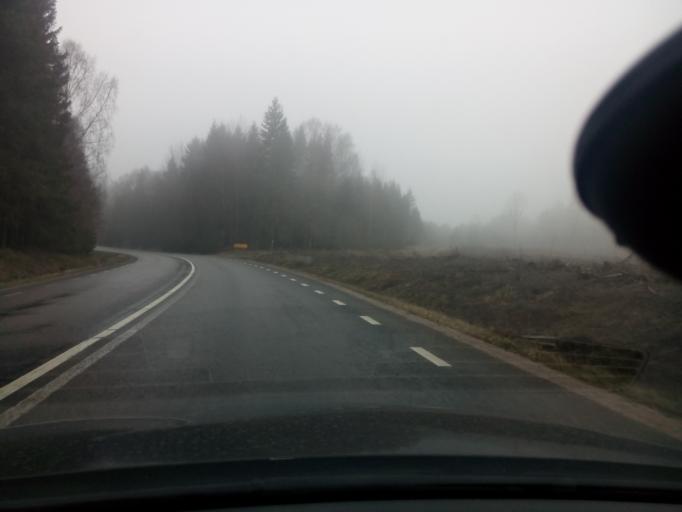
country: SE
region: Soedermanland
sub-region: Nykopings Kommun
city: Nykoping
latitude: 58.7908
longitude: 17.0756
